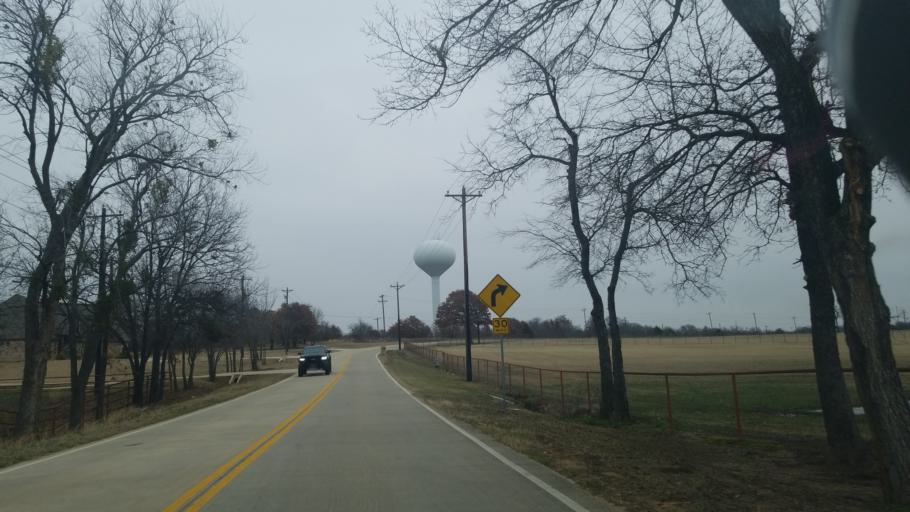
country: US
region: Texas
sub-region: Denton County
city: Copper Canyon
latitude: 33.1177
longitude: -97.1117
